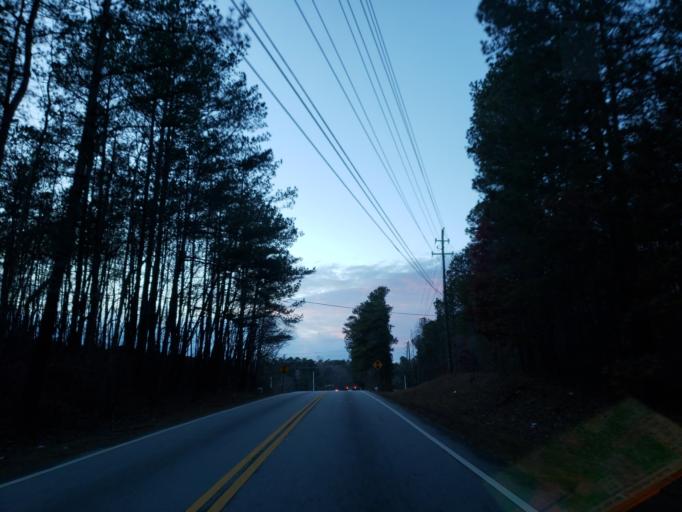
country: US
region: Georgia
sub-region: Douglas County
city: Lithia Springs
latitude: 33.6907
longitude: -84.6103
